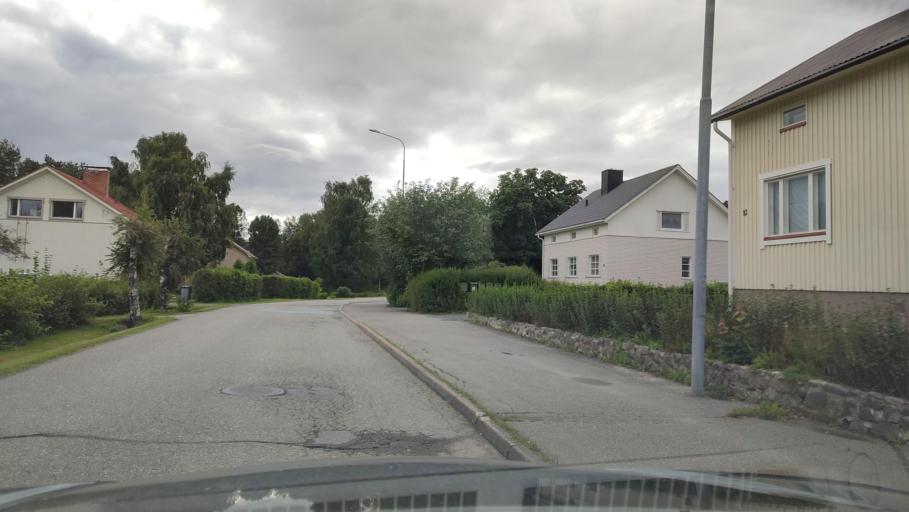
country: FI
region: Ostrobothnia
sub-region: Sydosterbotten
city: Kristinestad
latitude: 62.2712
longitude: 21.3714
